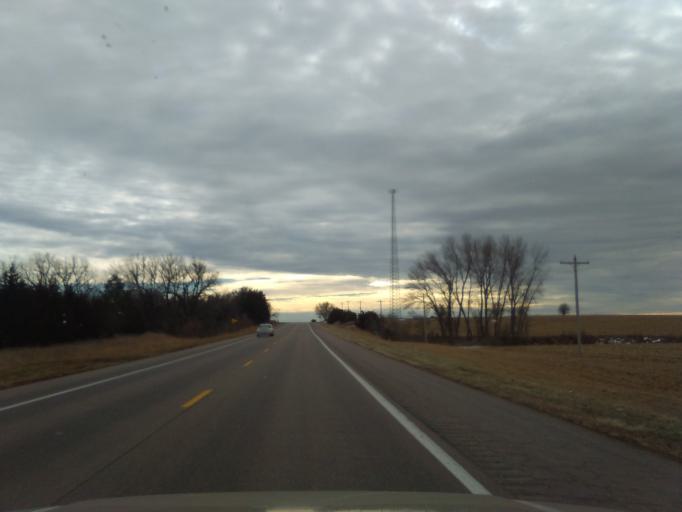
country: US
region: Nebraska
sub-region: Kearney County
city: Minden
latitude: 40.5792
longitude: -98.9519
